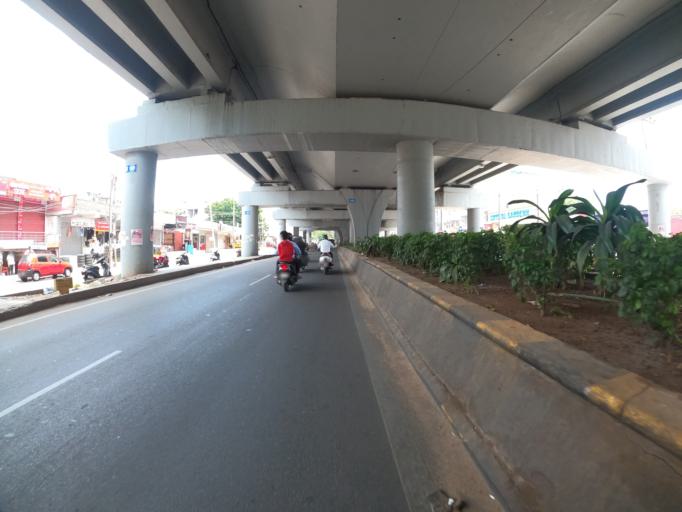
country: IN
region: Telangana
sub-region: Hyderabad
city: Hyderabad
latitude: 17.3816
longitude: 78.4294
